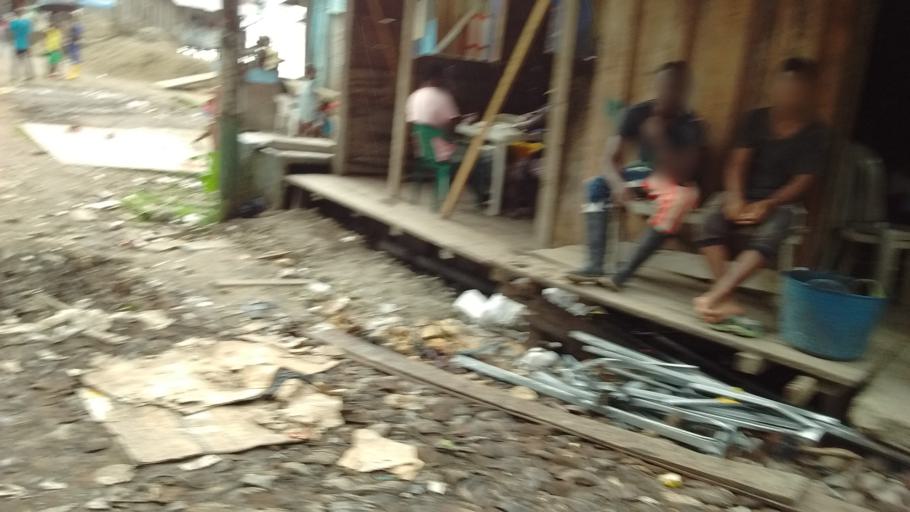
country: CO
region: Cauca
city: Guapi
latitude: 2.5724
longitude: -77.8838
